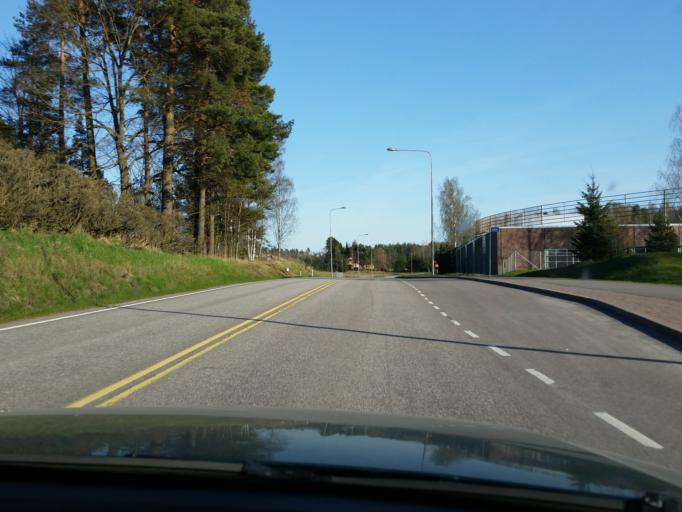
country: FI
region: Uusimaa
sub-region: Helsinki
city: Kirkkonummi
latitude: 60.1322
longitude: 24.5132
